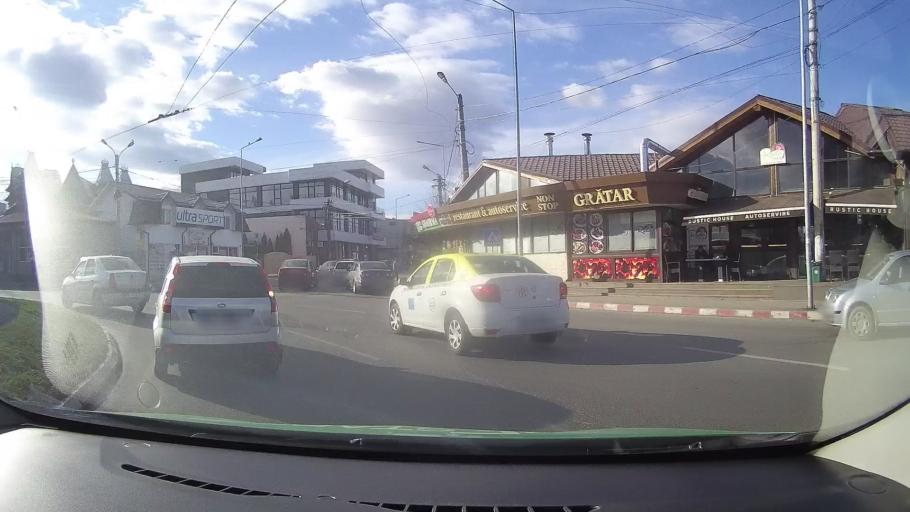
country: RO
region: Dambovita
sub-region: Comuna Lucieni
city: Lucieni
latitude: 44.8586
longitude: 25.4185
